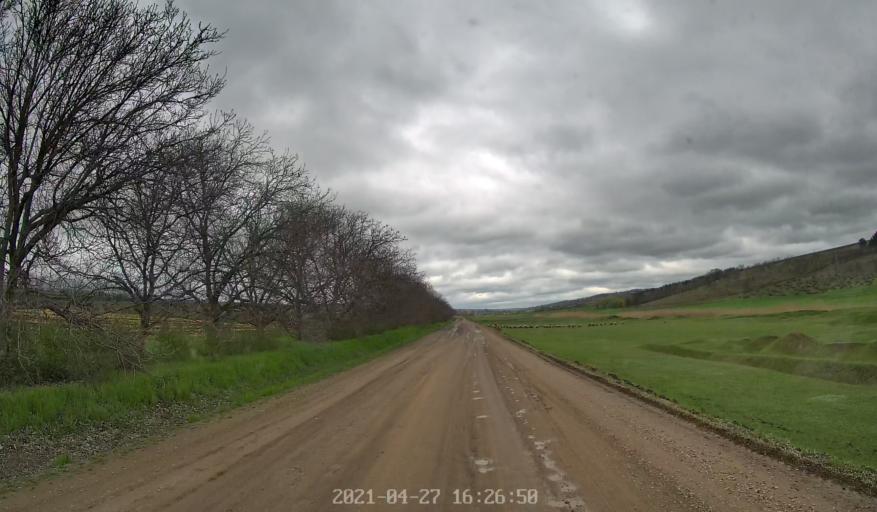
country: MD
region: Chisinau
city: Singera
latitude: 46.9778
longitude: 29.0293
